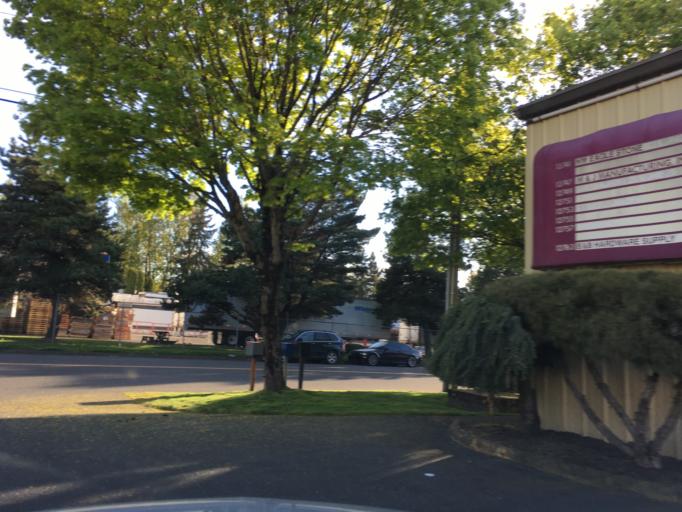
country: US
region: Oregon
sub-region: Multnomah County
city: Lents
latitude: 45.5608
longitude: -122.5311
